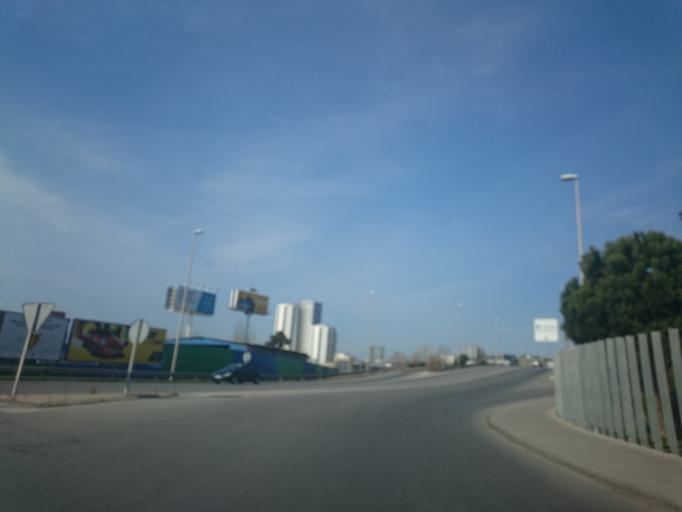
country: ES
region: Catalonia
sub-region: Provincia de Barcelona
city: L'Hospitalet de Llobregat
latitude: 41.3436
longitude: 2.1103
